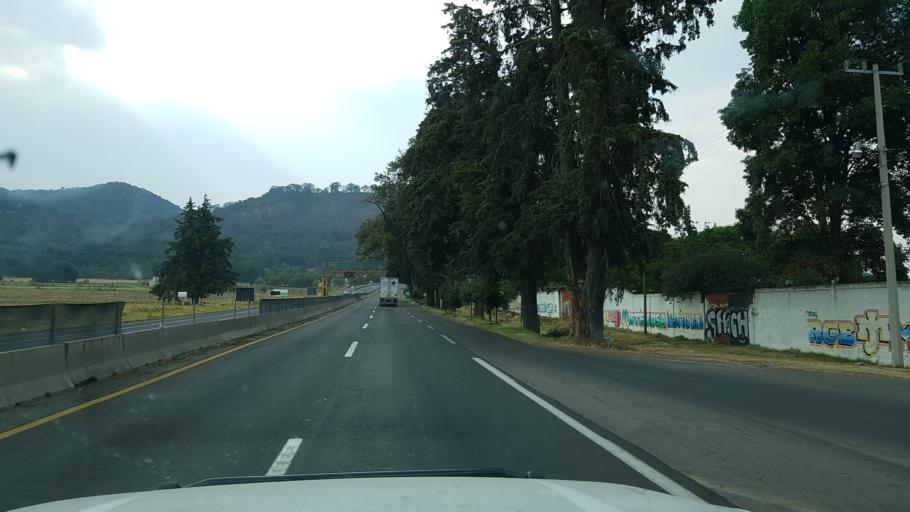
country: MX
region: Mexico
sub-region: Tlalmanalco
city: Santo Tomas Atzingo
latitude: 19.1700
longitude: -98.7847
